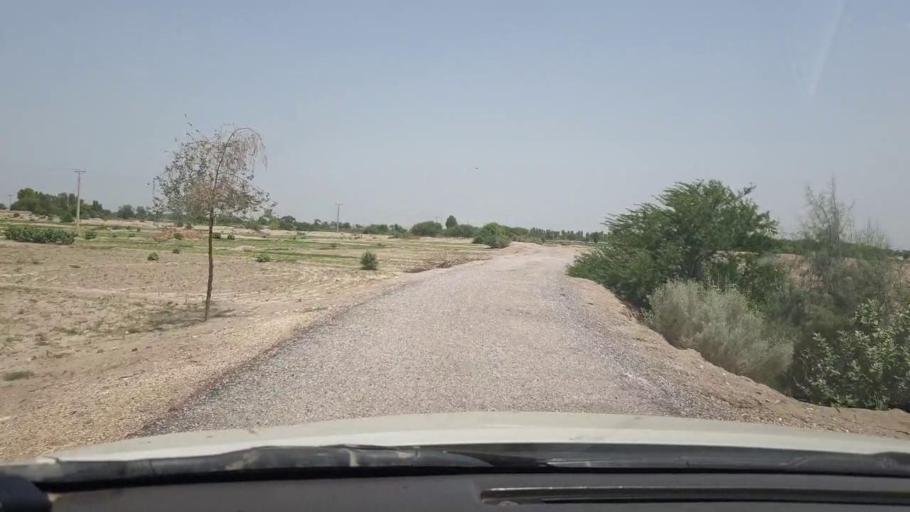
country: PK
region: Sindh
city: Rohri
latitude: 27.5297
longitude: 69.1570
